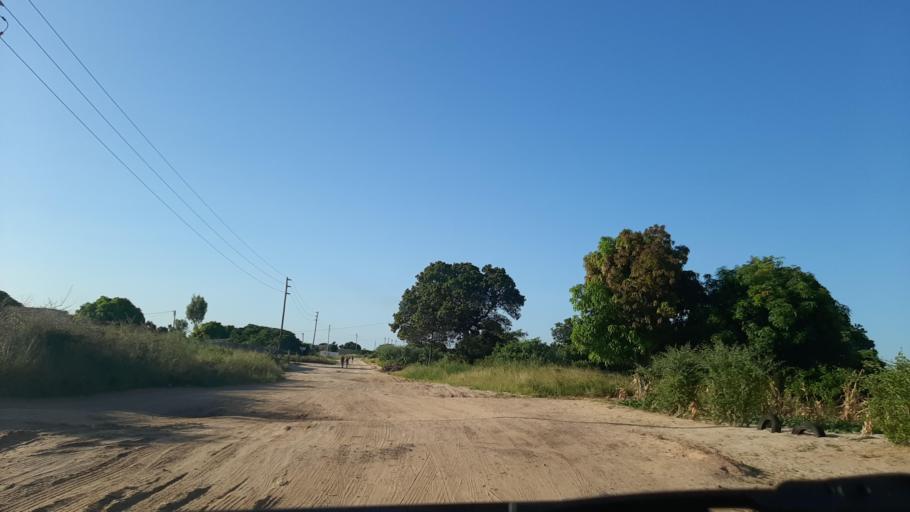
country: MZ
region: Maputo City
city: Maputo
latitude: -25.7572
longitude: 32.5504
